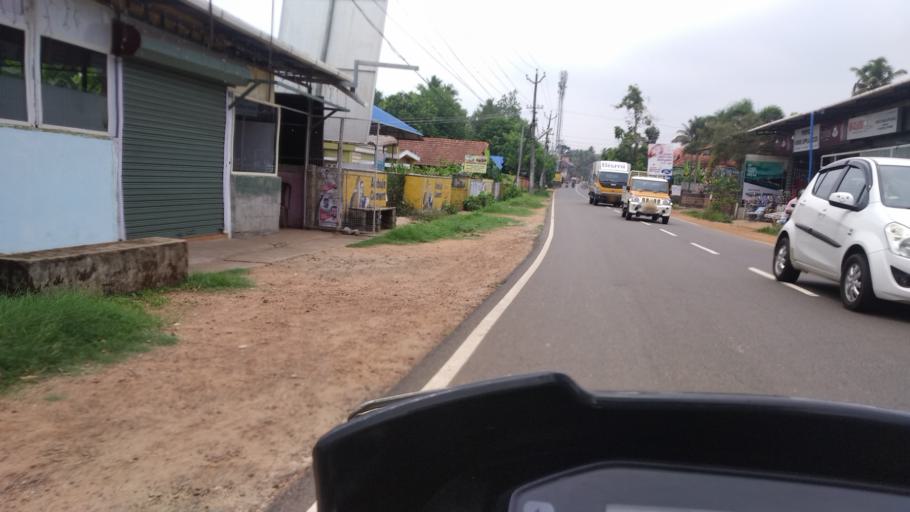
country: IN
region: Kerala
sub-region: Ernakulam
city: Aluva
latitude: 10.1560
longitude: 76.3292
